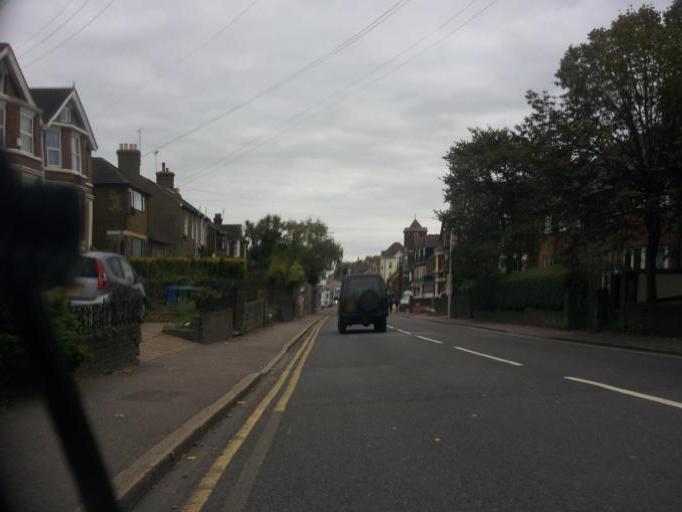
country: GB
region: England
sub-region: Kent
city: Sittingbourne
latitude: 51.3415
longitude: 0.7274
